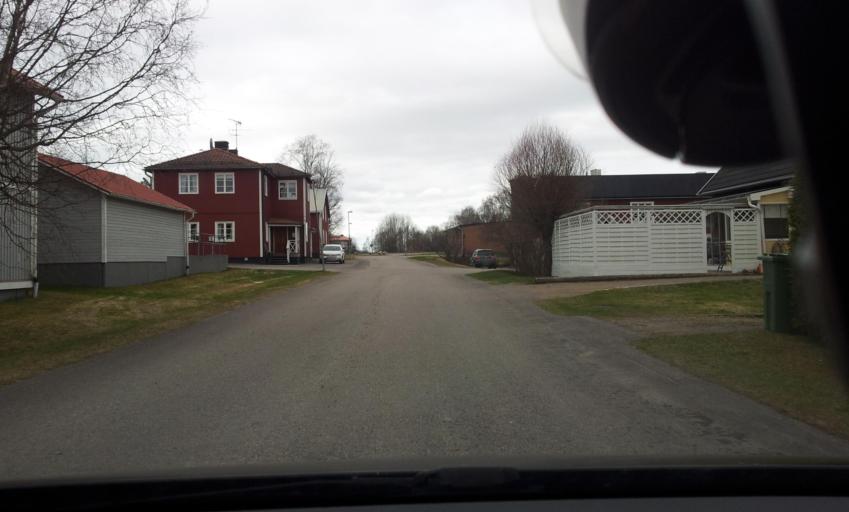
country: SE
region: Gaevleborg
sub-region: Ljusdals Kommun
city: Farila
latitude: 61.8024
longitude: 15.8502
